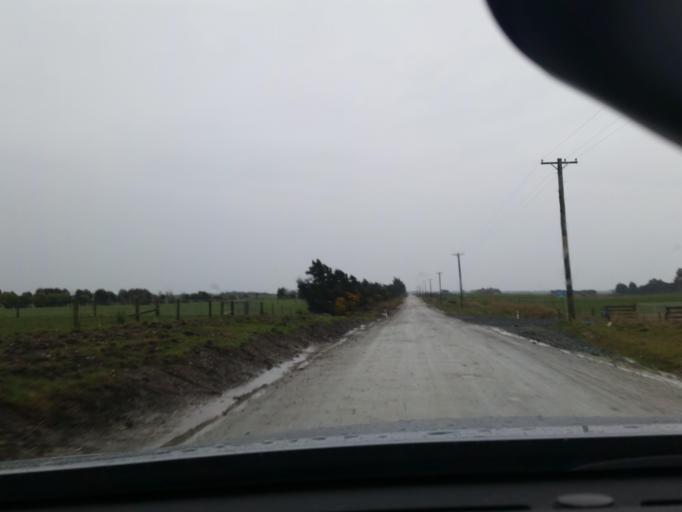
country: NZ
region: Southland
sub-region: Invercargill City
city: Invercargill
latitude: -46.4245
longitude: 168.5062
